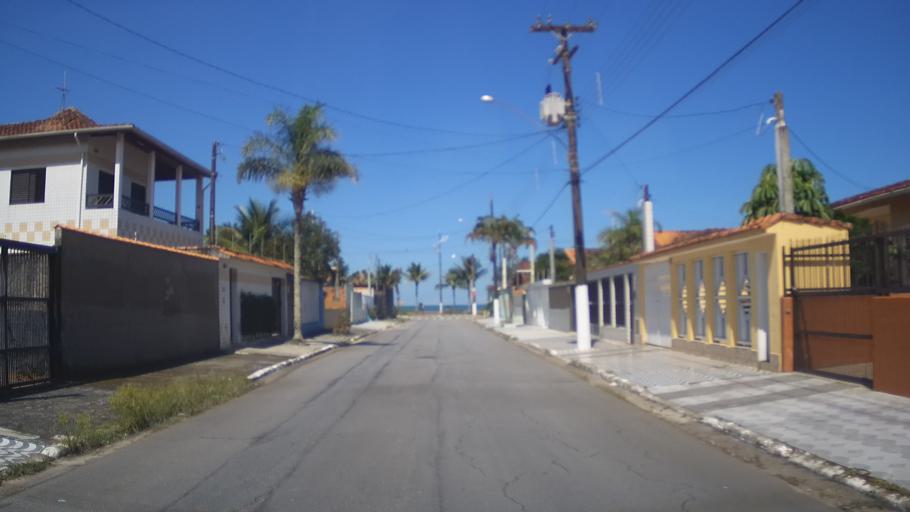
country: BR
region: Sao Paulo
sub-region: Mongagua
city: Mongagua
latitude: -24.0856
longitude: -46.6010
